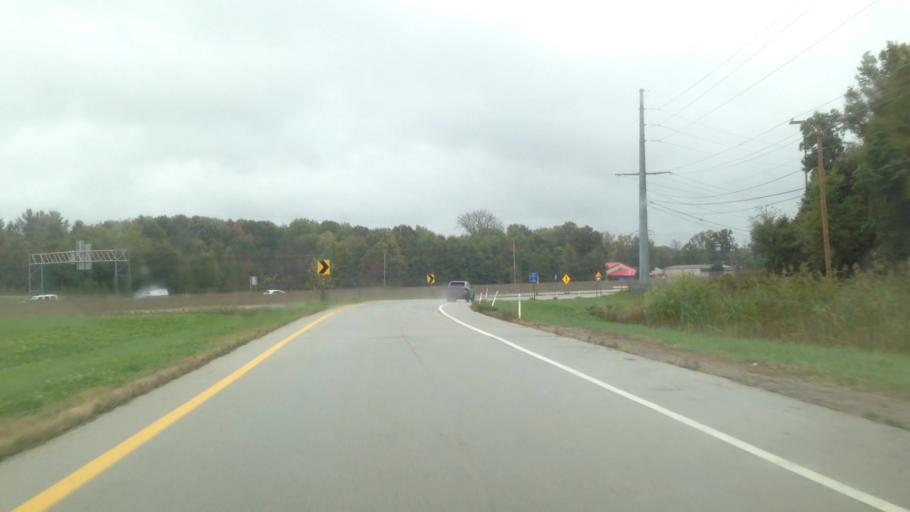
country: US
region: Ohio
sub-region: Summit County
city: Boston Heights
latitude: 41.2532
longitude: -81.5012
